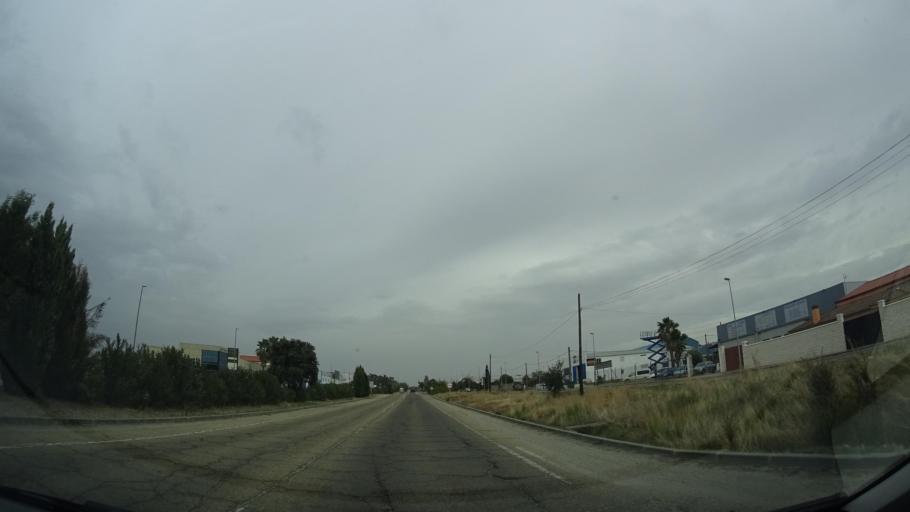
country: ES
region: Extremadura
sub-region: Provincia de Caceres
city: Trujillo
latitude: 39.4754
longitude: -5.8583
